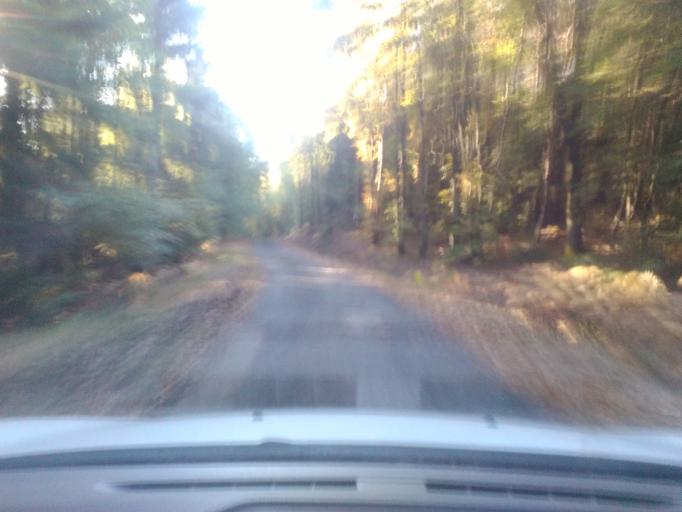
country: FR
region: Lorraine
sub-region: Departement des Vosges
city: Jeanmenil
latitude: 48.2859
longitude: 6.7218
